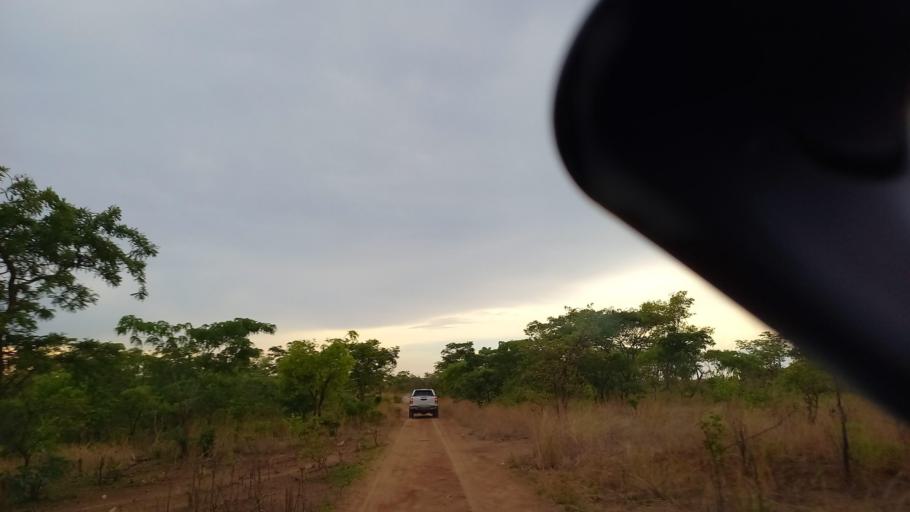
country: ZM
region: Lusaka
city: Kafue
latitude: -16.0485
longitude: 28.3300
